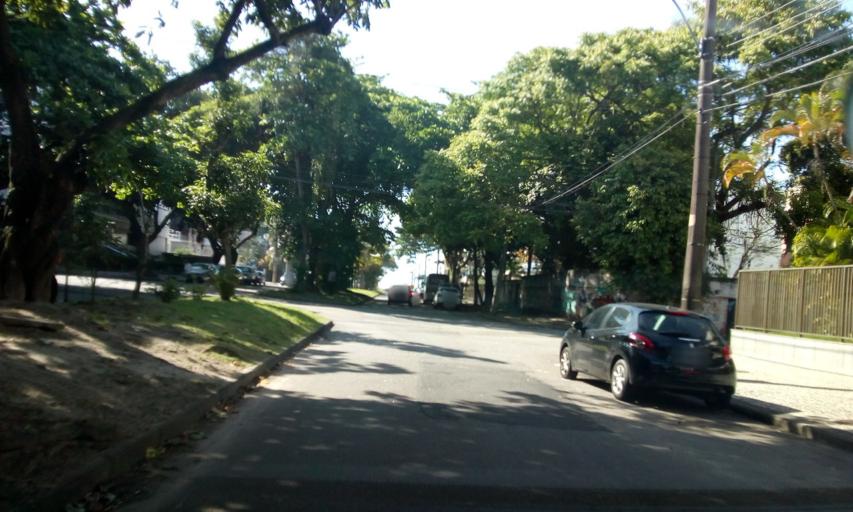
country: BR
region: Rio de Janeiro
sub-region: Rio De Janeiro
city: Rio de Janeiro
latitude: -23.0130
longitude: -43.3079
